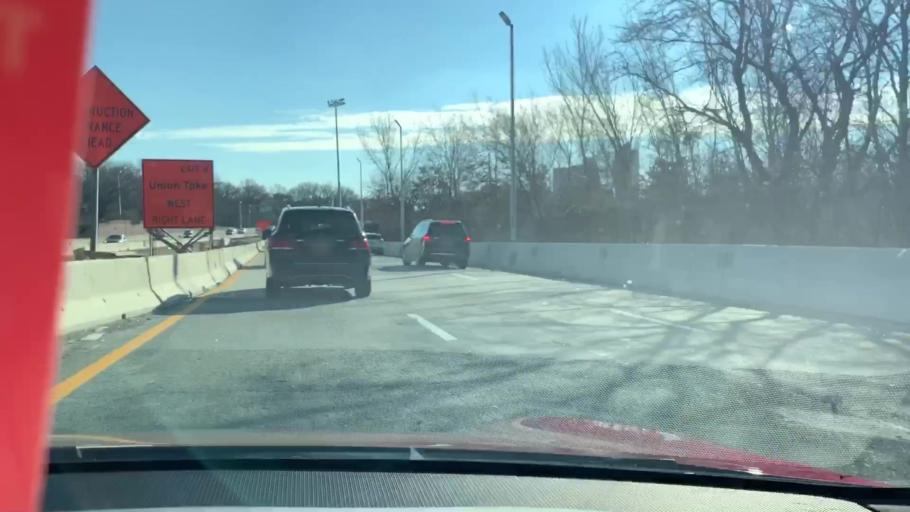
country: US
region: New York
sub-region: Queens County
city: Jamaica
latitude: 40.7223
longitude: -73.8274
